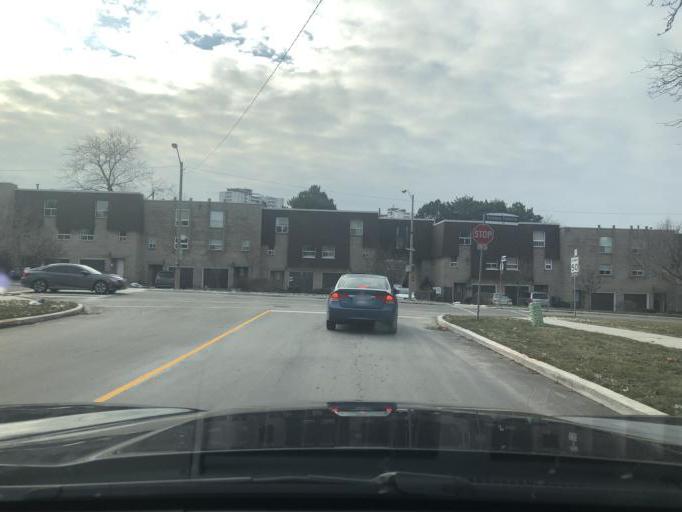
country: CA
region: Ontario
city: Willowdale
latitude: 43.7697
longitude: -79.3436
